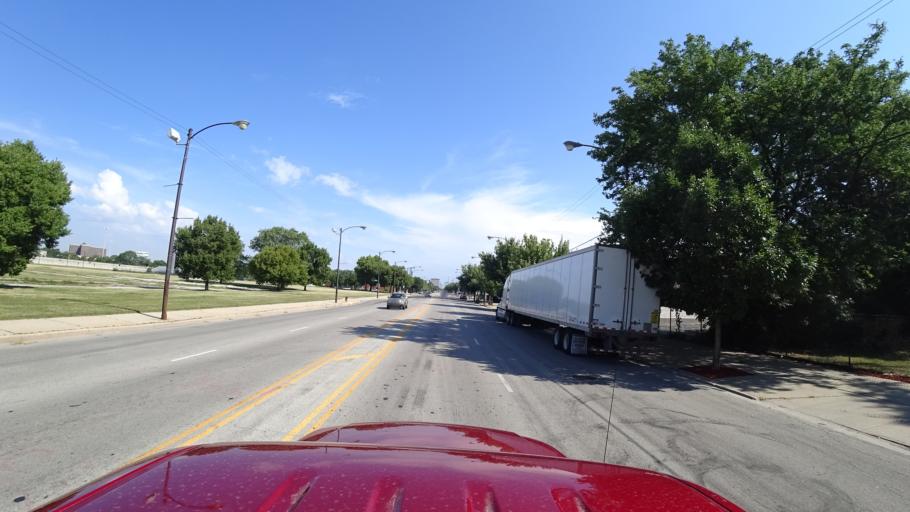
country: US
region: Illinois
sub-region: Cook County
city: Chicago
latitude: 41.8116
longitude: -87.6261
